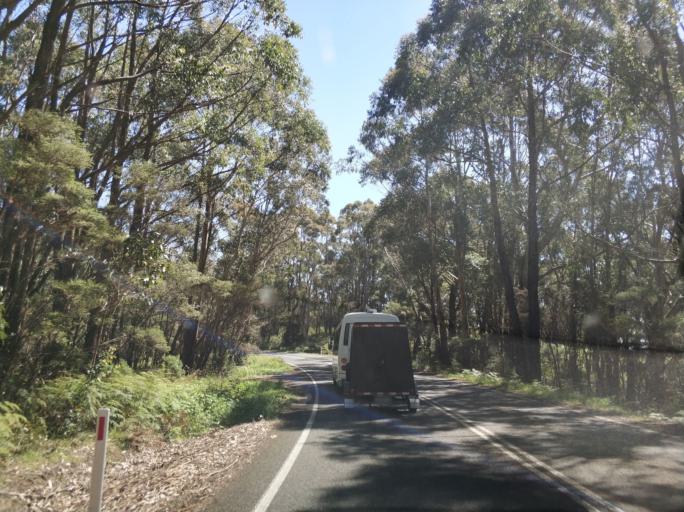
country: AU
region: Victoria
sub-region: Colac-Otway
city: Apollo Bay
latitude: -38.7459
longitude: 143.2656
